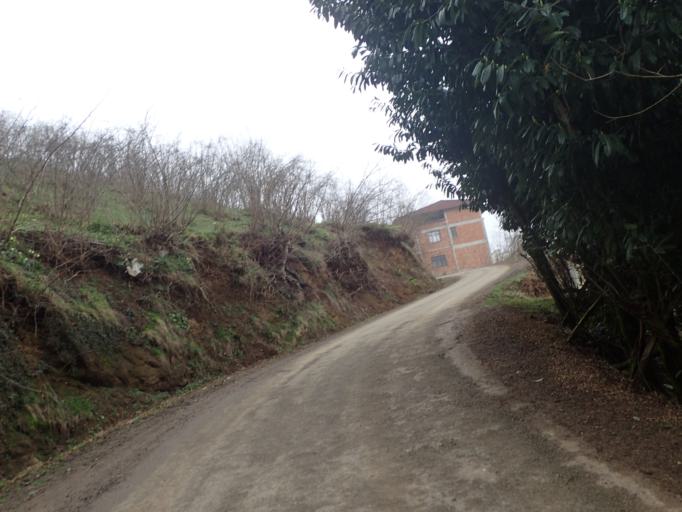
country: TR
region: Ordu
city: Camas
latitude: 40.9223
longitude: 37.5535
